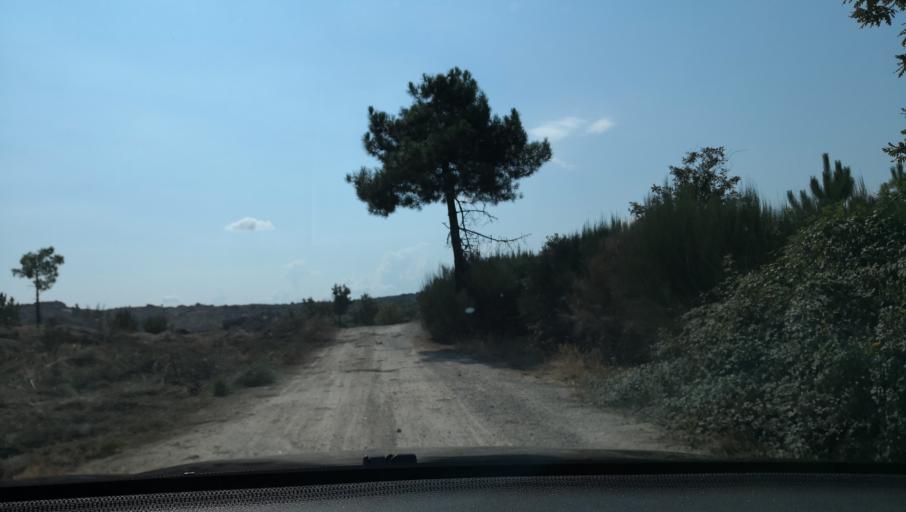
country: PT
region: Vila Real
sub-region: Sabrosa
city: Sabrosa
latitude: 41.3190
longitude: -7.6201
